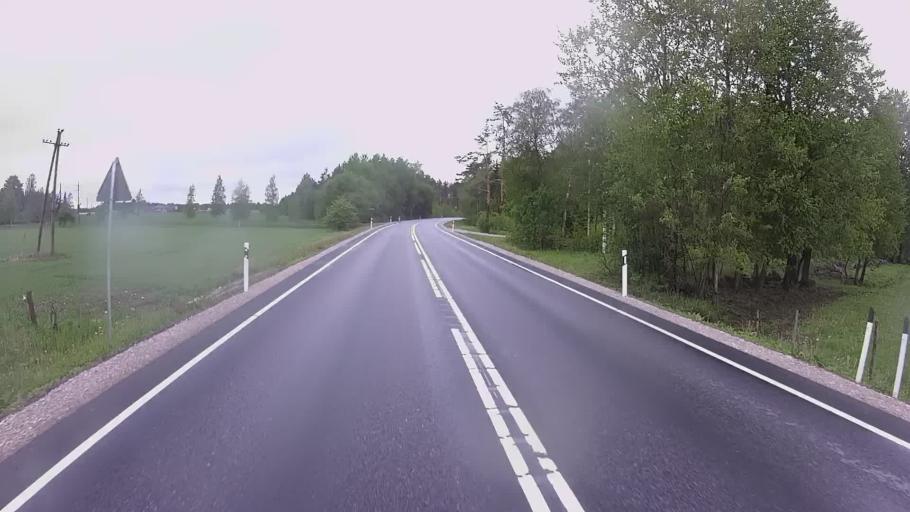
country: EE
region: Raplamaa
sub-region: Maerjamaa vald
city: Marjamaa
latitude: 58.9203
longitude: 24.2943
